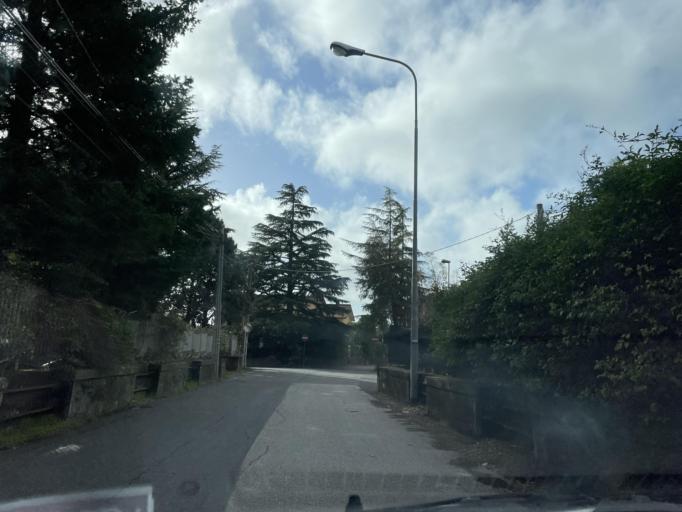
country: IT
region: Sicily
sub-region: Catania
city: Nicolosi
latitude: 37.6204
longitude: 15.0243
